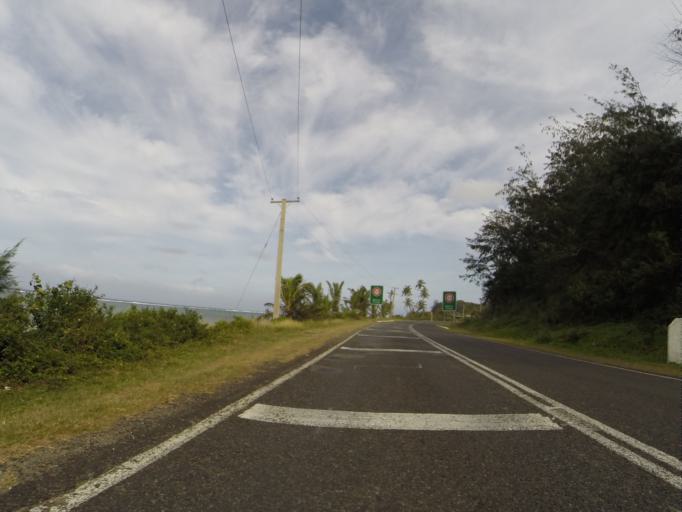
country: FJ
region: Western
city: Nadi
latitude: -18.1803
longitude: 177.5608
